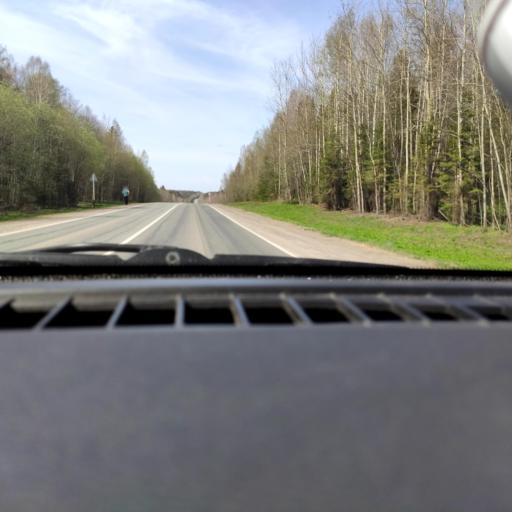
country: RU
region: Perm
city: Perm
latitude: 58.1520
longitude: 56.2553
